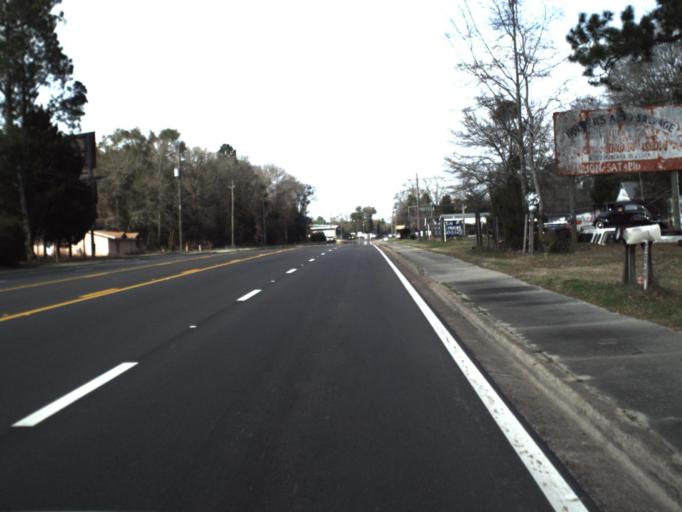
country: US
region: Florida
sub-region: Bay County
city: Youngstown
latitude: 30.3722
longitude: -85.4383
